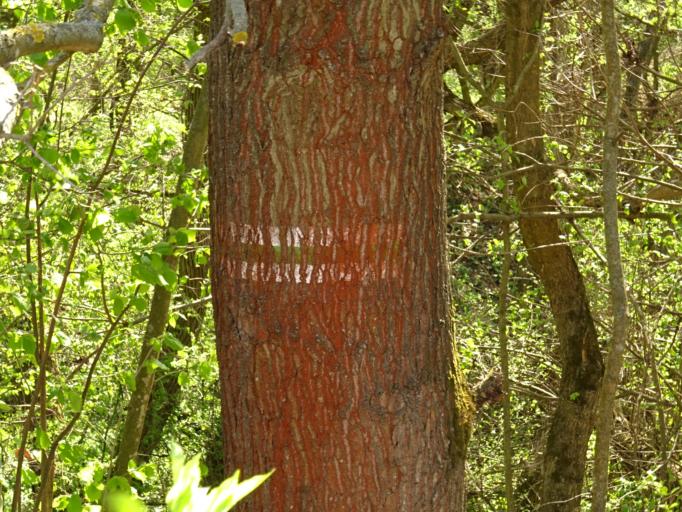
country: HU
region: Borsod-Abauj-Zemplen
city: Gonc
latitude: 48.5476
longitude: 21.3286
